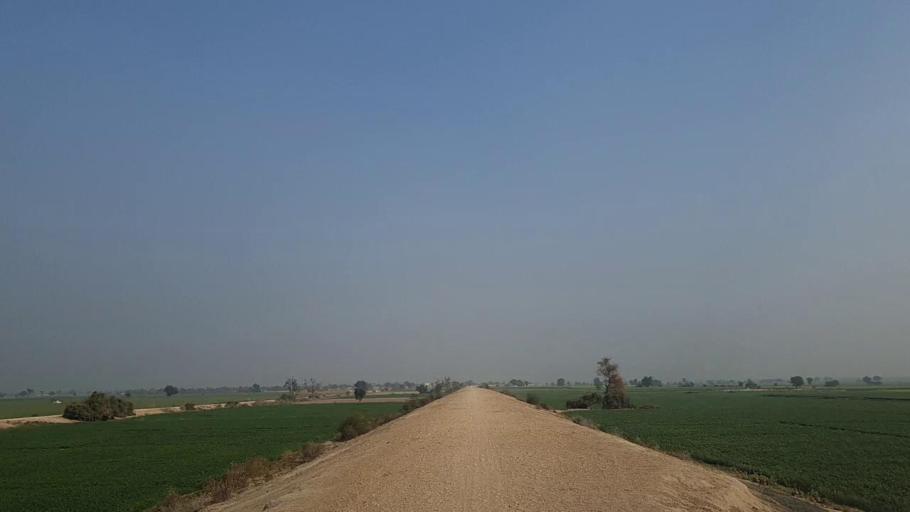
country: PK
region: Sindh
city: Sann
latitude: 26.0848
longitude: 68.1688
